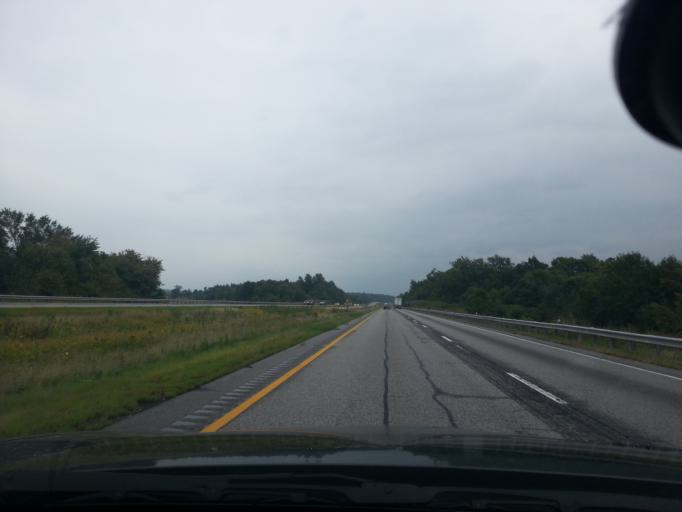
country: CA
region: Ontario
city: Gananoque
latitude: 44.3688
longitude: -76.0609
